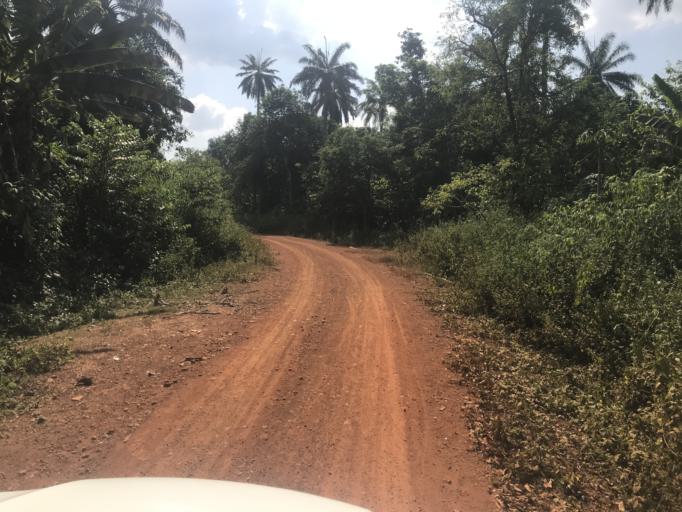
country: NG
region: Osun
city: Ibokun
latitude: 7.8134
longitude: 4.6966
